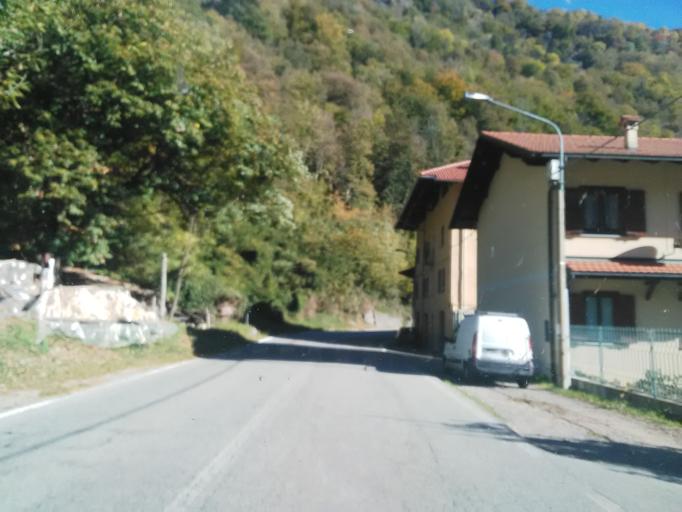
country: IT
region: Piedmont
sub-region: Provincia di Vercelli
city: Varallo
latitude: 45.8205
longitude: 8.2380
